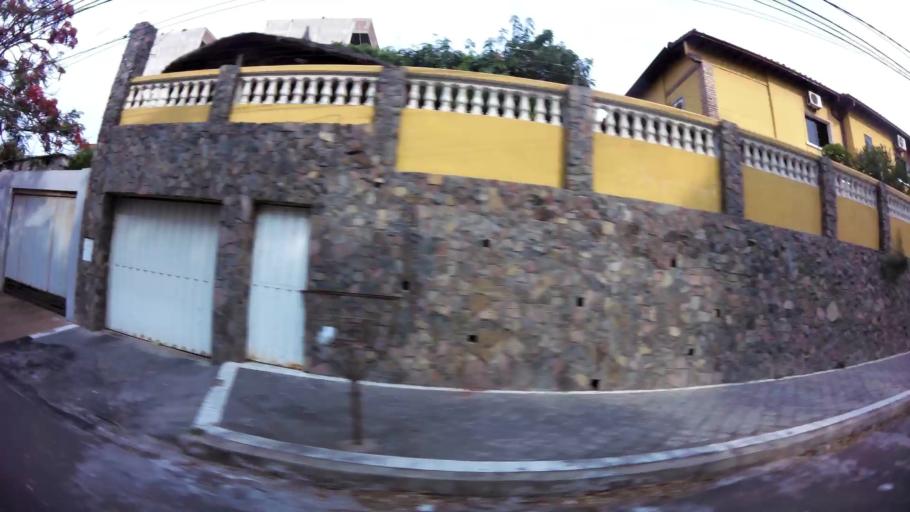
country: PY
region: Asuncion
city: Asuncion
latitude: -25.2947
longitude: -57.6153
